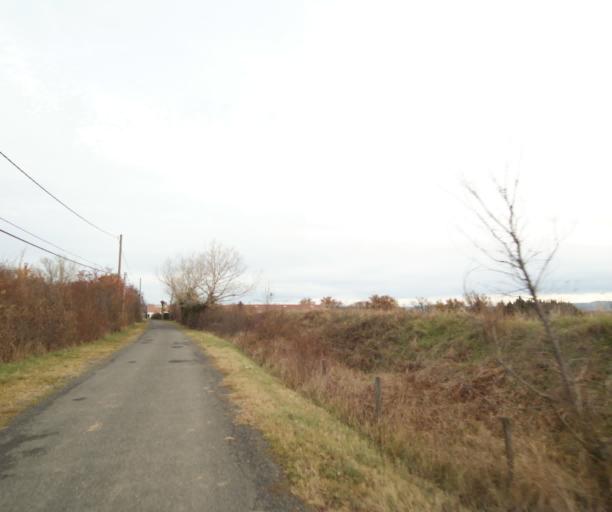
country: FR
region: Rhone-Alpes
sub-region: Departement de la Loire
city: Sury-le-Comtal
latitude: 45.5277
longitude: 4.1925
